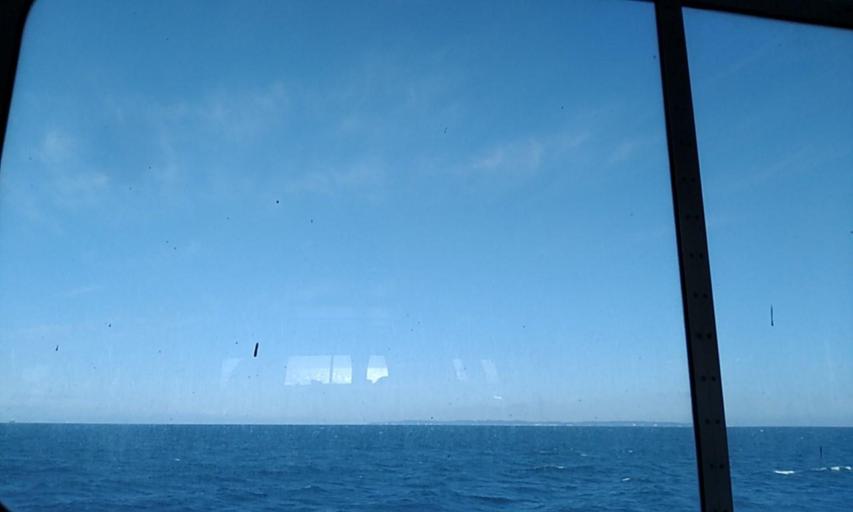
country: JP
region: Aichi
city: Toyohama
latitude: 34.5761
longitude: 136.9843
